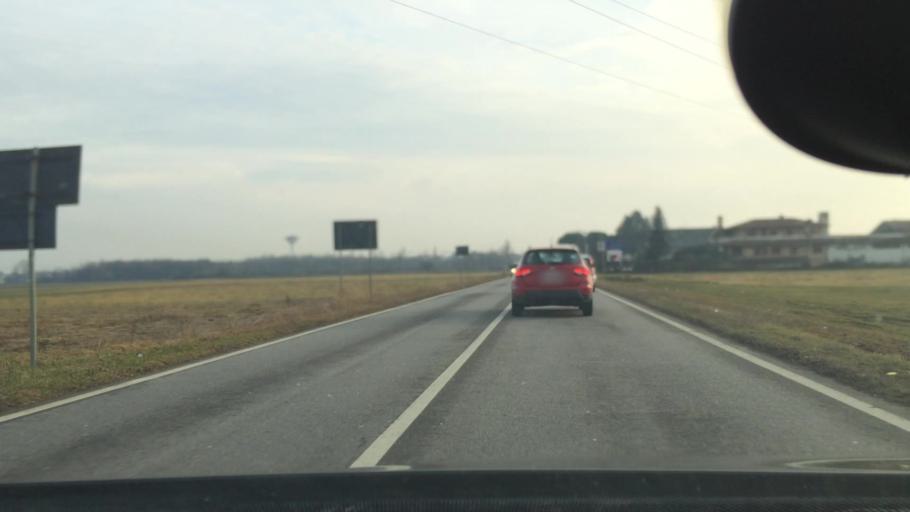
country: IT
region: Lombardy
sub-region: Provincia di Varese
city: Origgio
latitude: 45.5877
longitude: 9.0243
